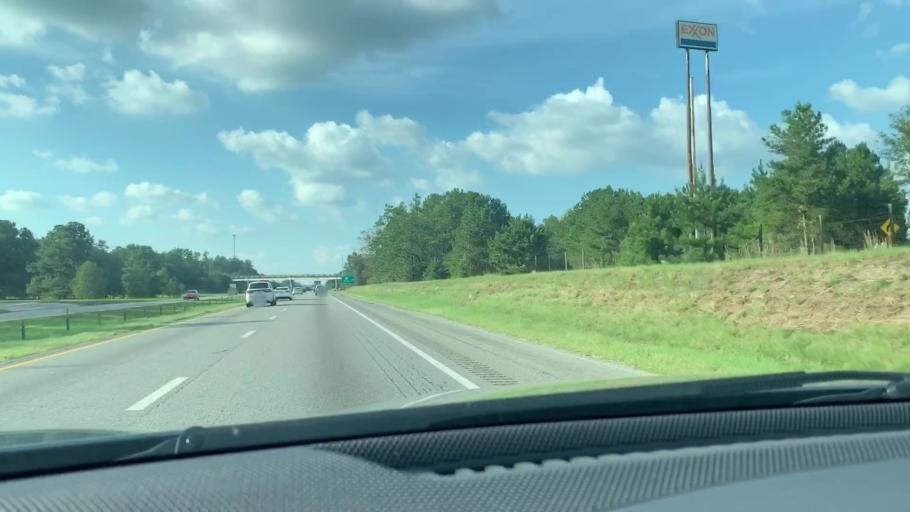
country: US
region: South Carolina
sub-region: Calhoun County
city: Saint Matthews
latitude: 33.6699
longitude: -80.8959
